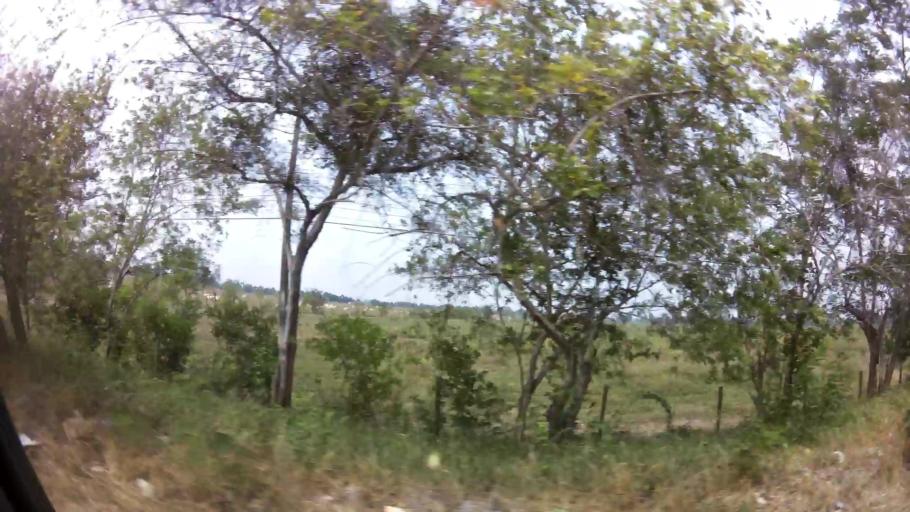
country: HN
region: Cortes
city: La Lima
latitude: 15.4220
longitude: -87.8961
